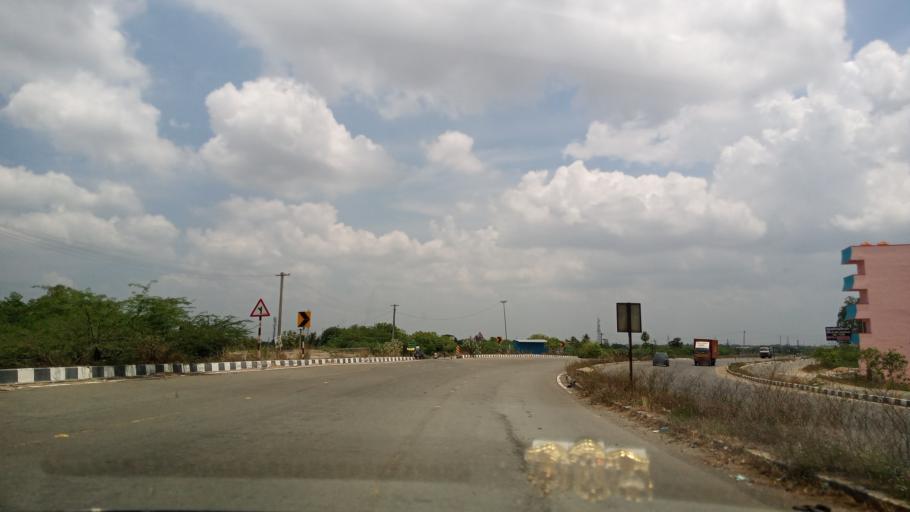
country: IN
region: Tamil Nadu
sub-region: Kancheepuram
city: Sriperumbudur
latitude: 12.9195
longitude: 79.9319
